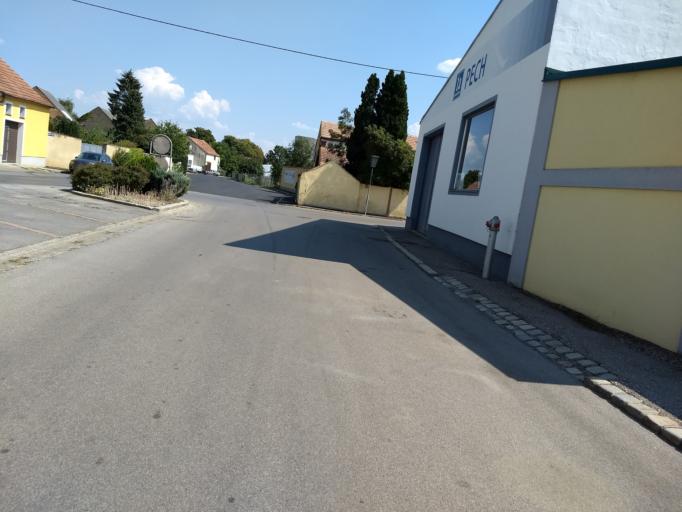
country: AT
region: Lower Austria
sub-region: Politischer Bezirk Mistelbach
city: Poysdorf
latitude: 48.6681
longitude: 16.6316
